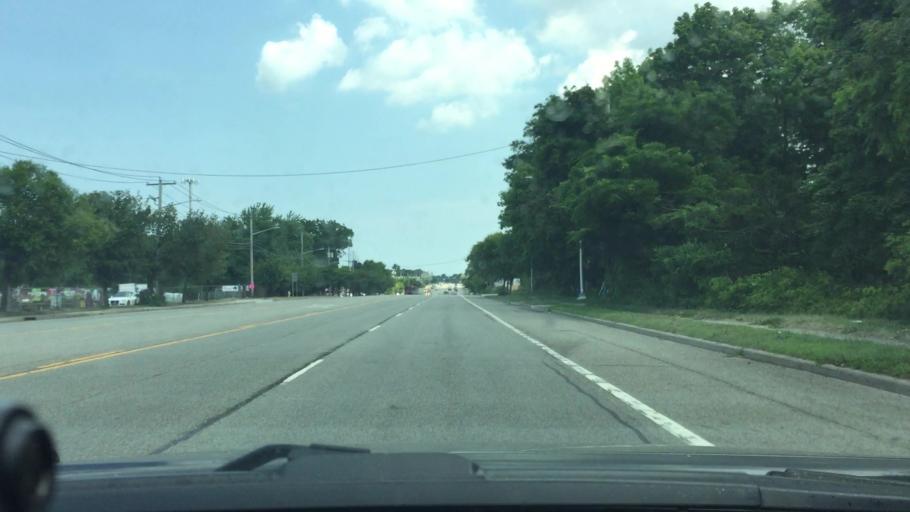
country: US
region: New York
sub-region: Suffolk County
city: Mount Sinai
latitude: 40.9333
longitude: -73.0280
